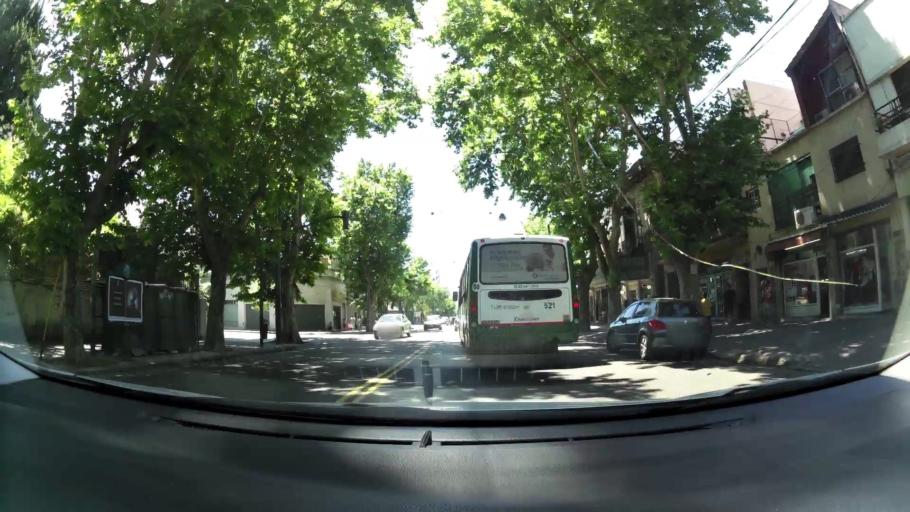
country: AR
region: Buenos Aires F.D.
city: Buenos Aires
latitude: -34.6343
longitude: -58.3912
